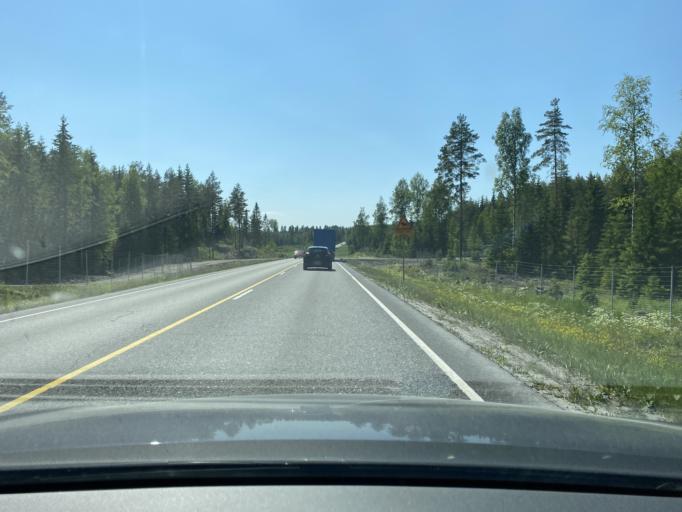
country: FI
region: Pirkanmaa
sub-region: Lounais-Pirkanmaa
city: Mouhijaervi
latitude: 61.3929
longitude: 23.2272
